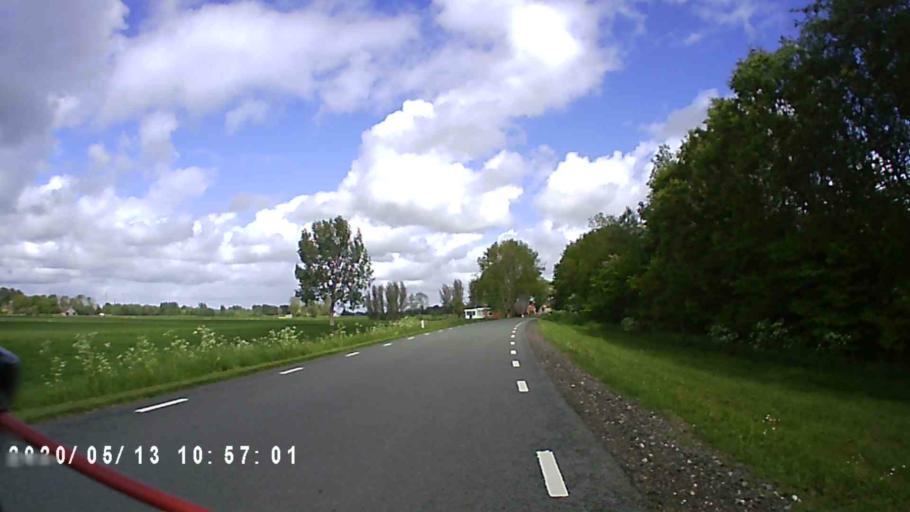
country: NL
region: Groningen
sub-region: Gemeente Zuidhorn
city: Grijpskerk
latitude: 53.2717
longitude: 6.3342
